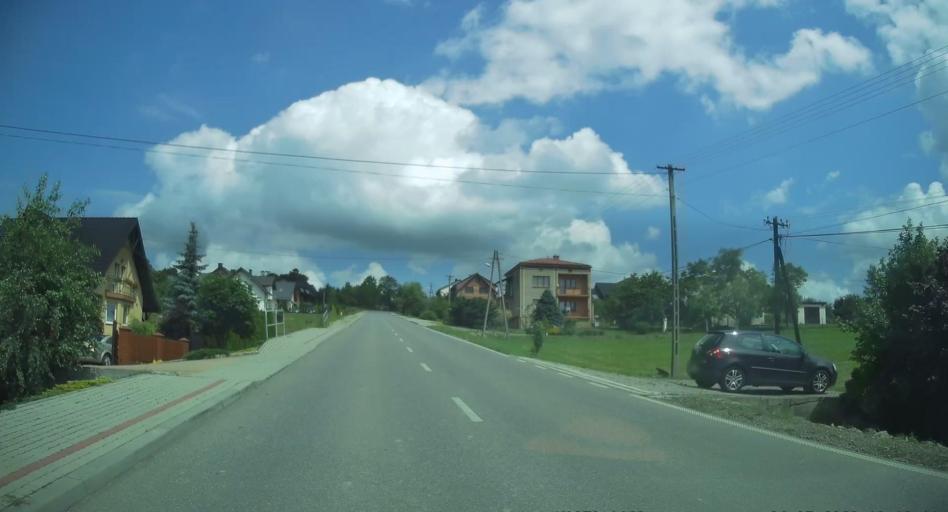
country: PL
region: Lesser Poland Voivodeship
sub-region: Powiat nowosadecki
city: Korzenna
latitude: 49.6849
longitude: 20.7754
